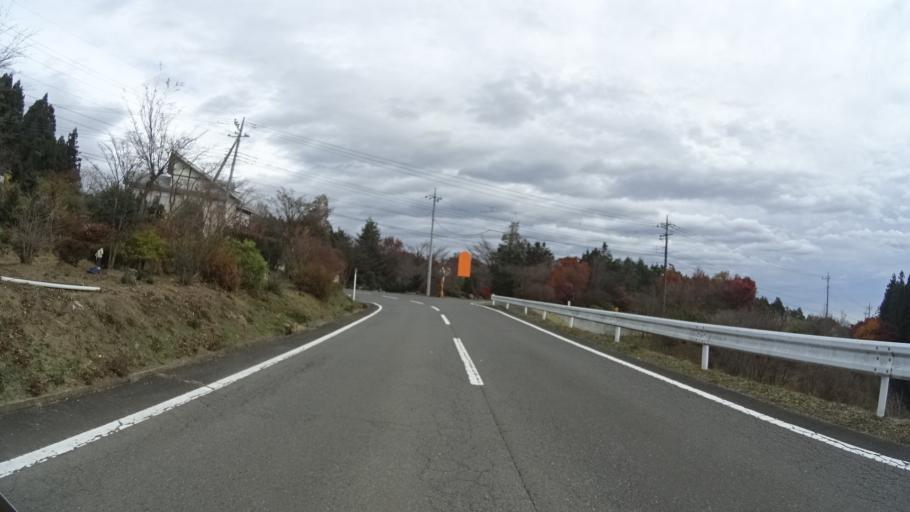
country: JP
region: Gunma
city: Maebashi-shi
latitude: 36.4756
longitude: 139.1484
